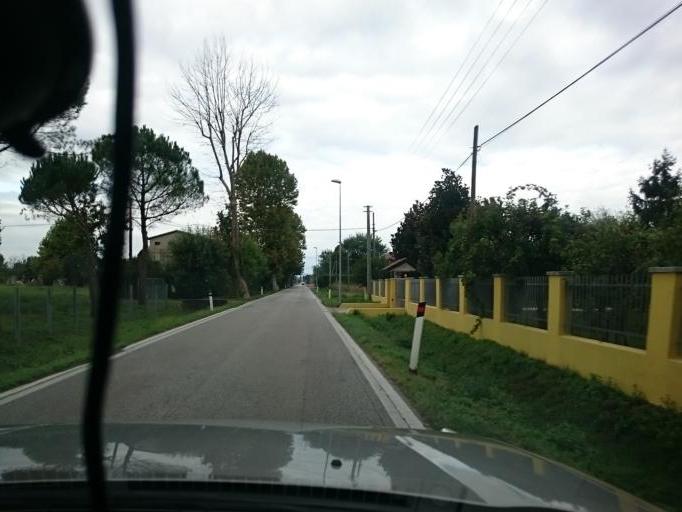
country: IT
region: Veneto
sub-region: Provincia di Padova
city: Mestrino
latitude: 45.4271
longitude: 11.7481
